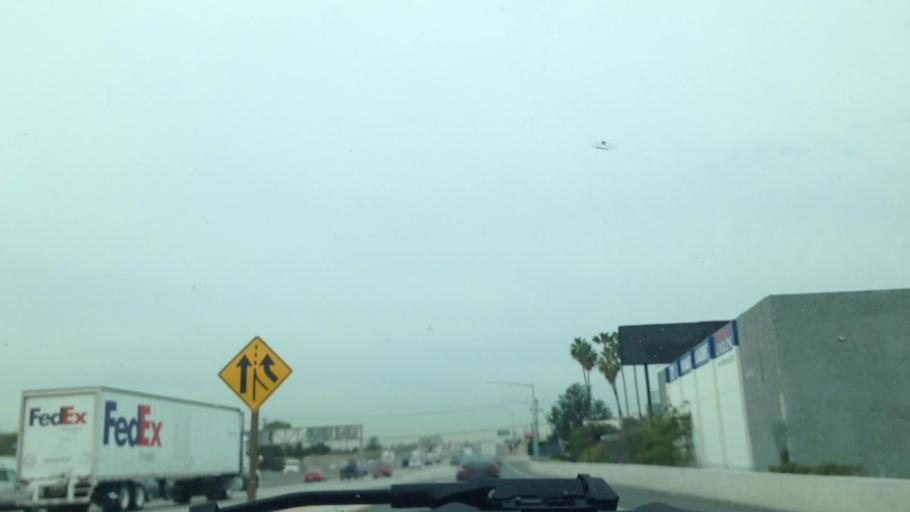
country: US
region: California
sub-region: Orange County
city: Placentia
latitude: 33.8545
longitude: -117.8913
